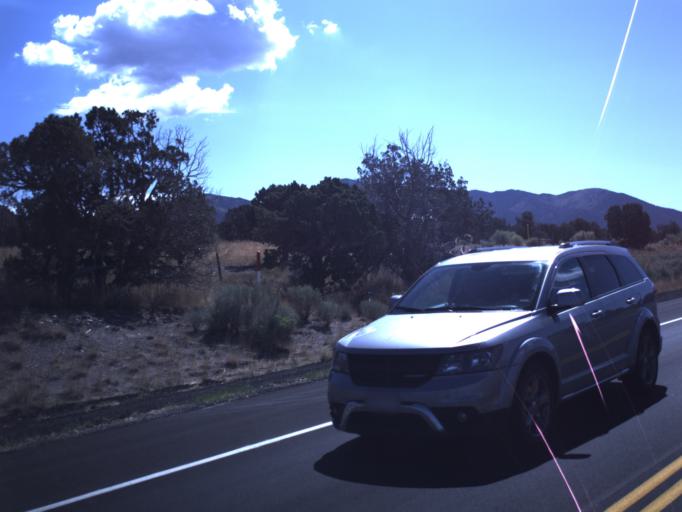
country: US
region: Utah
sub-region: Utah County
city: Eagle Mountain
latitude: 40.0454
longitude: -112.2930
